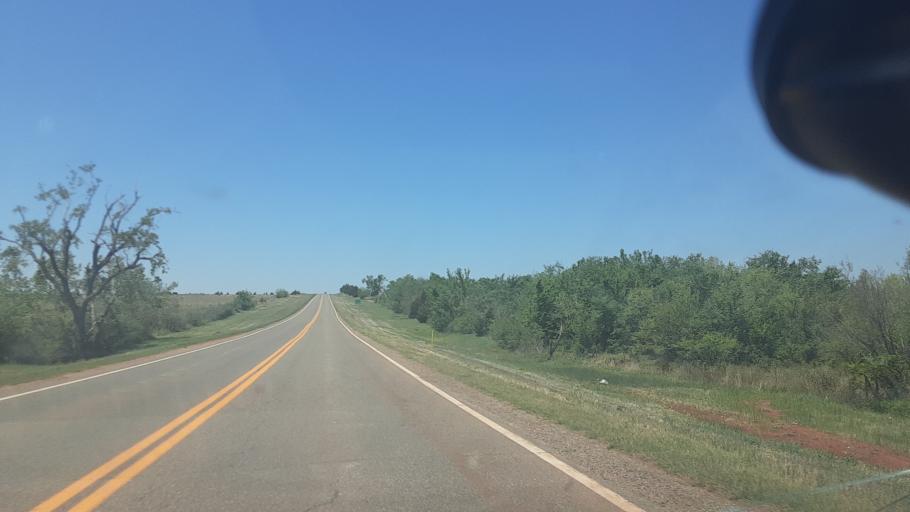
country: US
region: Oklahoma
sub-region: Noble County
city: Perry
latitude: 36.1157
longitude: -97.3544
